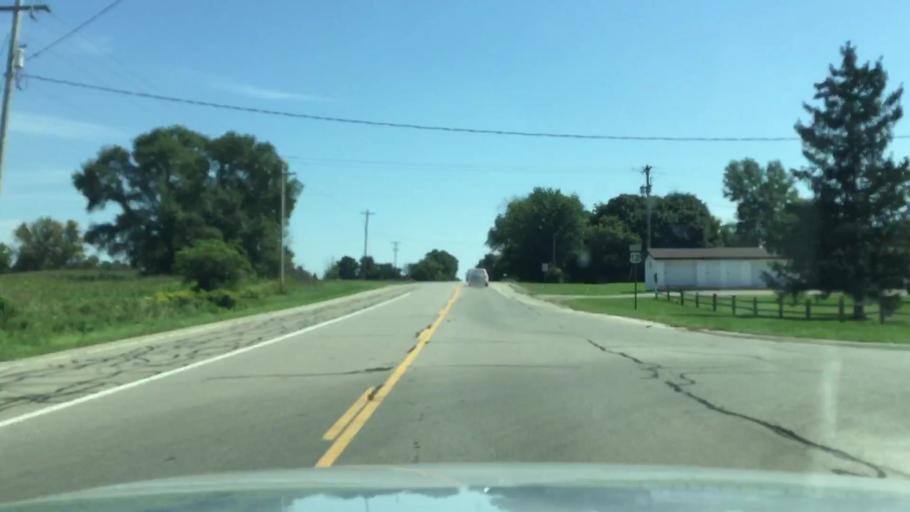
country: US
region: Michigan
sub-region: Washtenaw County
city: Manchester
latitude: 42.0726
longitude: -84.0667
